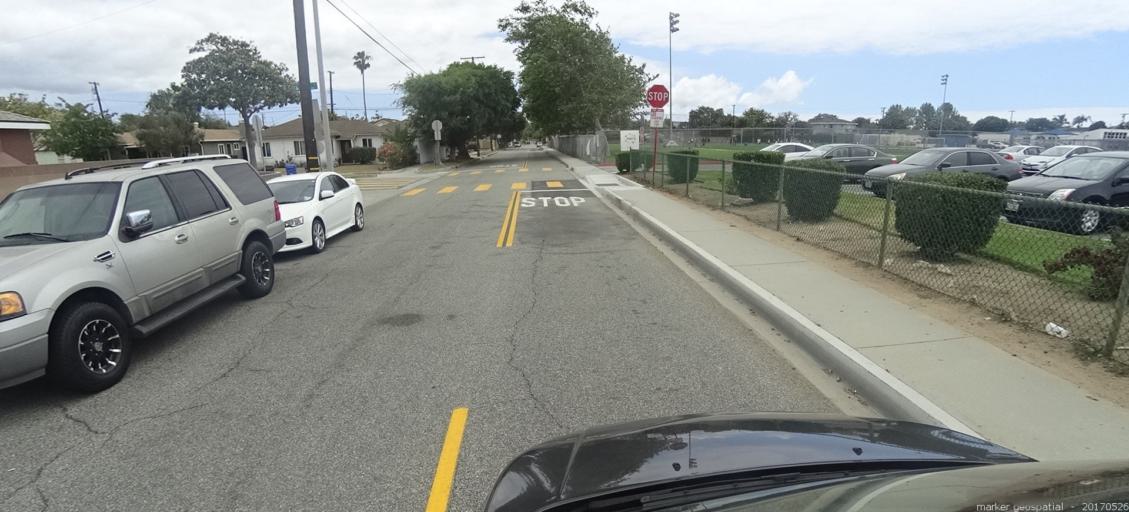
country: US
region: California
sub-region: Los Angeles County
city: Lawndale
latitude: 33.8651
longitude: -118.3631
